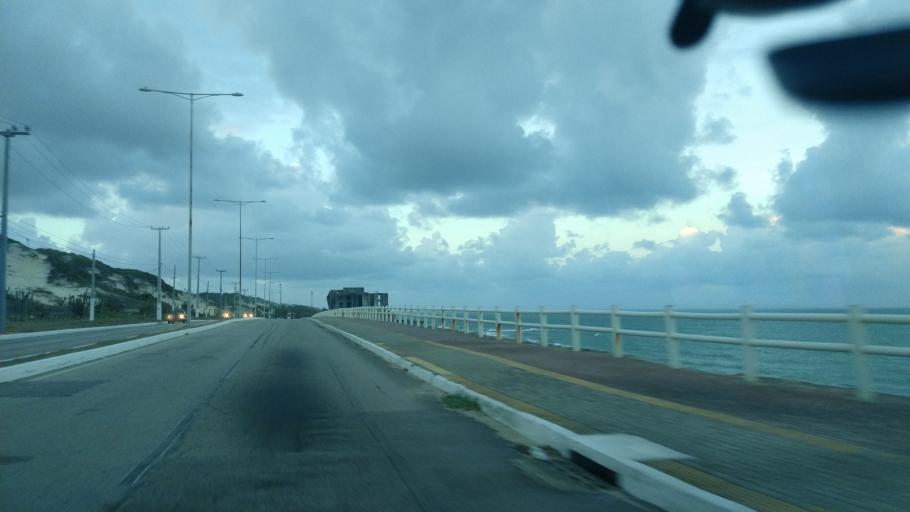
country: BR
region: Rio Grande do Norte
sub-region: Natal
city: Natal
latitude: -5.8374
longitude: -35.1824
